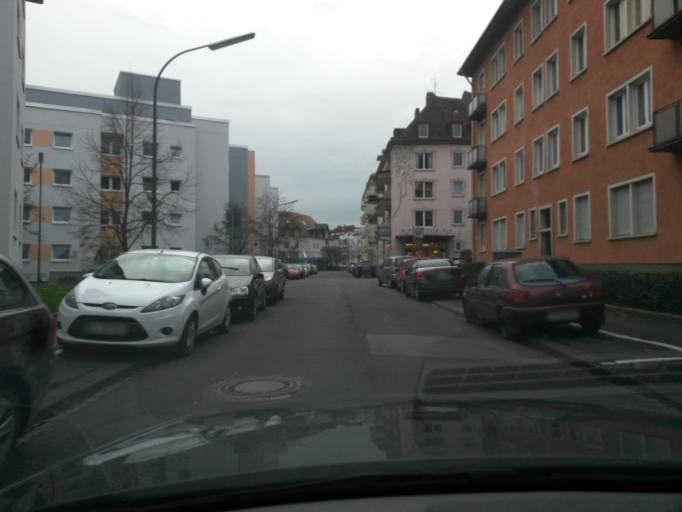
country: DE
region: Bavaria
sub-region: Regierungsbezirk Unterfranken
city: Wuerzburg
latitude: 49.7838
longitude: 9.9323
